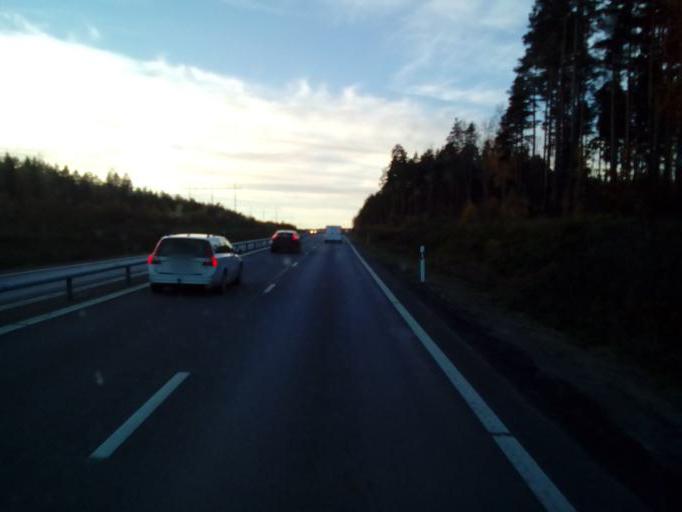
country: SE
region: OErebro
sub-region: Orebro Kommun
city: Orebro
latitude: 59.2067
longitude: 15.2140
